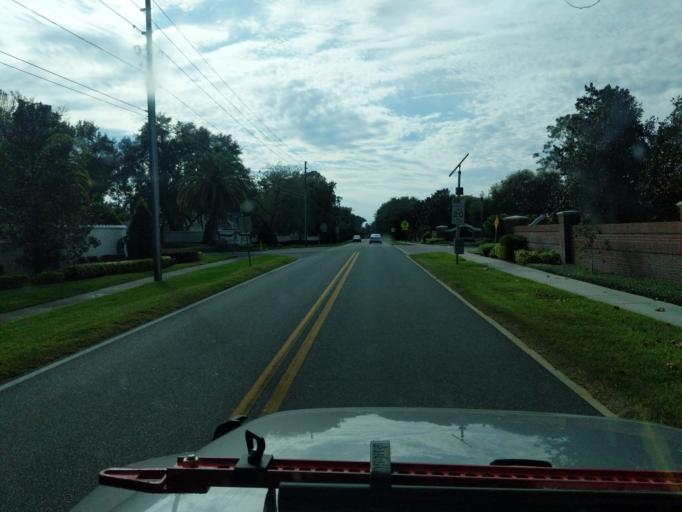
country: US
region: Florida
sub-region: Orange County
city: Gotha
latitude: 28.5226
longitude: -81.5324
